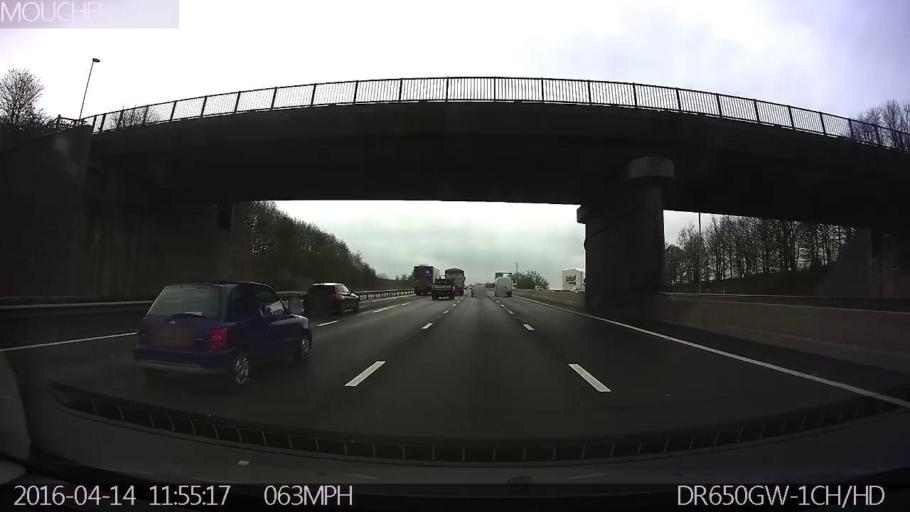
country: GB
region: England
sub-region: Derbyshire
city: Tibshelf
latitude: 53.1468
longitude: -1.3304
